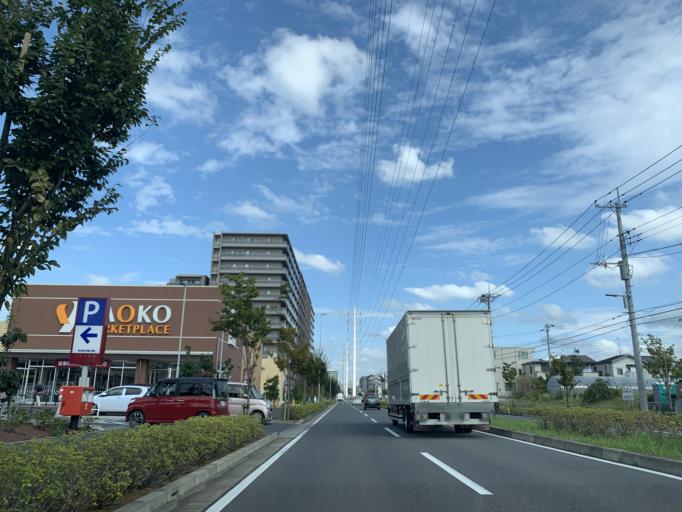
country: JP
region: Chiba
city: Nagareyama
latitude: 35.8643
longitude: 139.9206
